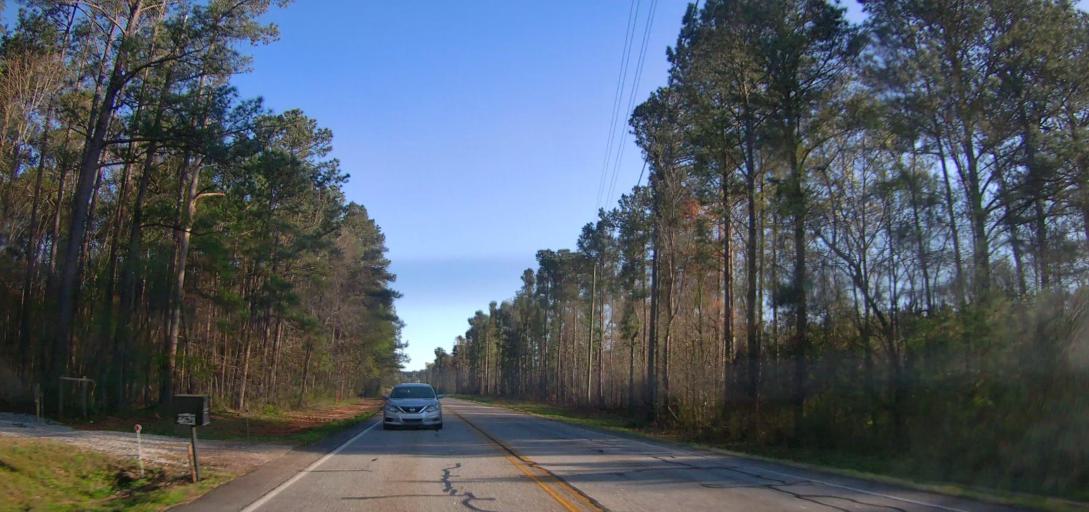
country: US
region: Georgia
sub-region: Newton County
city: Oakwood
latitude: 33.4483
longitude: -83.9033
